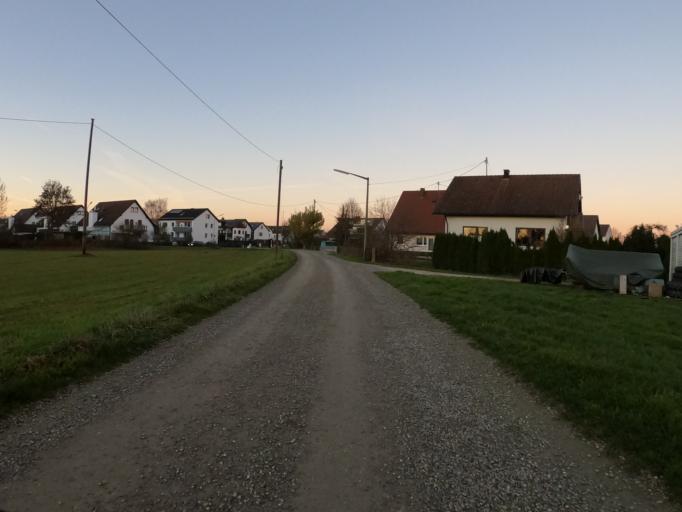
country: DE
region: Bavaria
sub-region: Swabia
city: Nersingen
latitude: 48.4288
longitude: 10.1105
